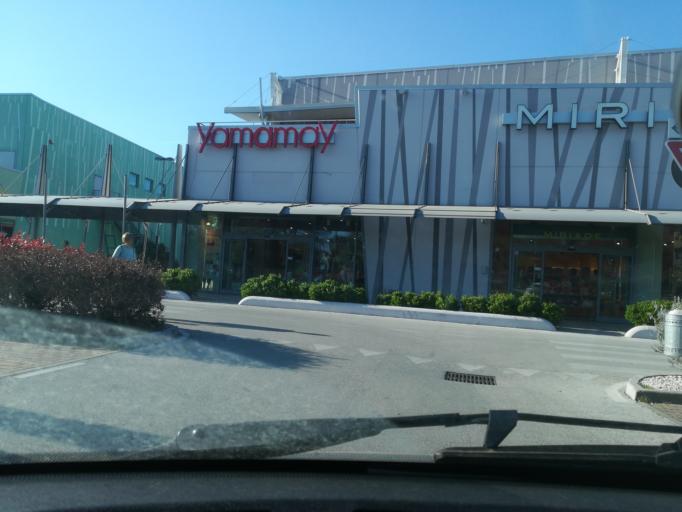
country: IT
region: The Marches
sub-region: Provincia di Macerata
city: Piediripa
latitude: 43.2699
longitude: 13.4829
